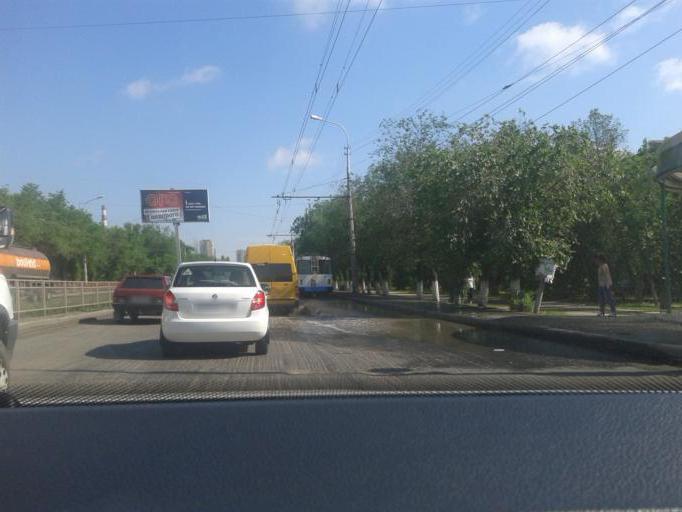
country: RU
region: Volgograd
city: Volgograd
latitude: 48.6071
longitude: 44.4222
